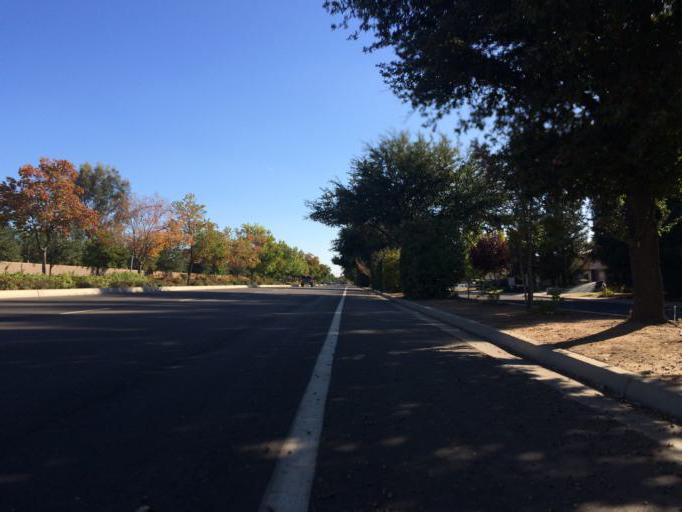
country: US
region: California
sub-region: Fresno County
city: Clovis
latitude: 36.8261
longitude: -119.6640
